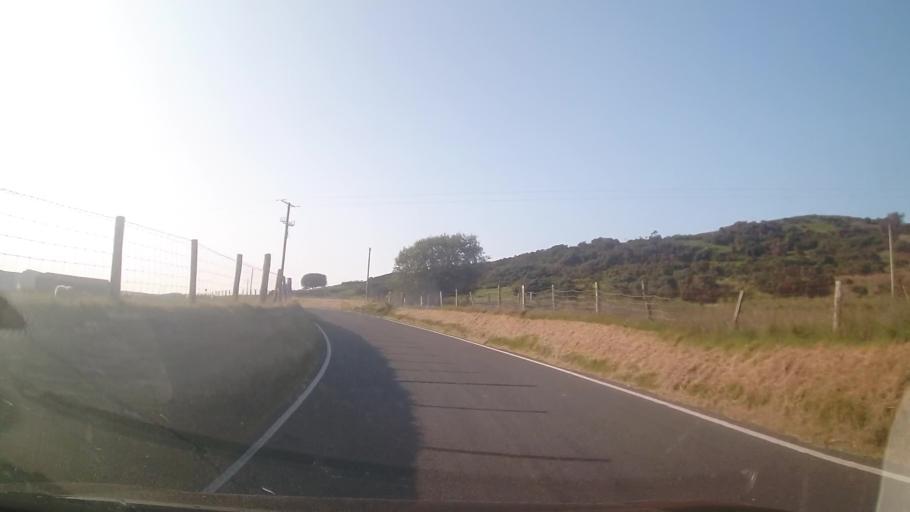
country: GB
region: Wales
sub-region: County of Ceredigion
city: Lledrod
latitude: 52.3121
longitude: -3.8549
